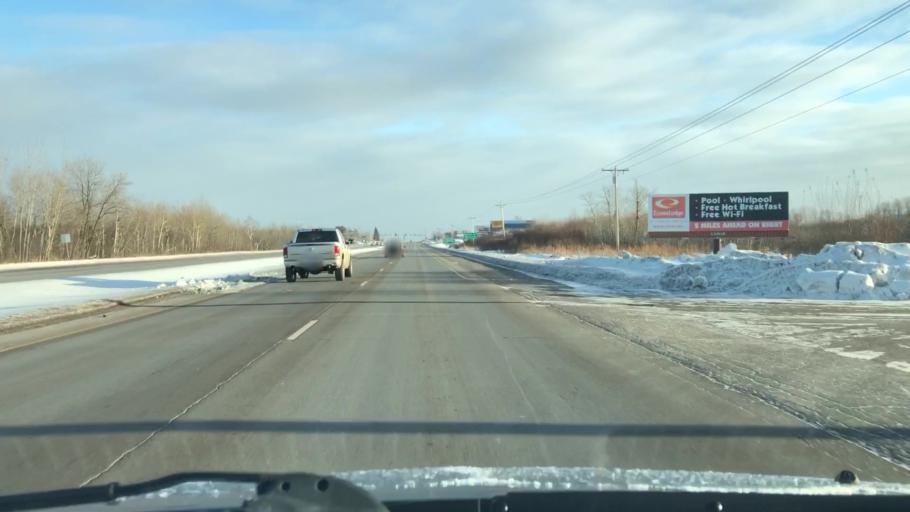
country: US
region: Minnesota
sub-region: Saint Louis County
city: Hermantown
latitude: 46.8314
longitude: -92.2020
